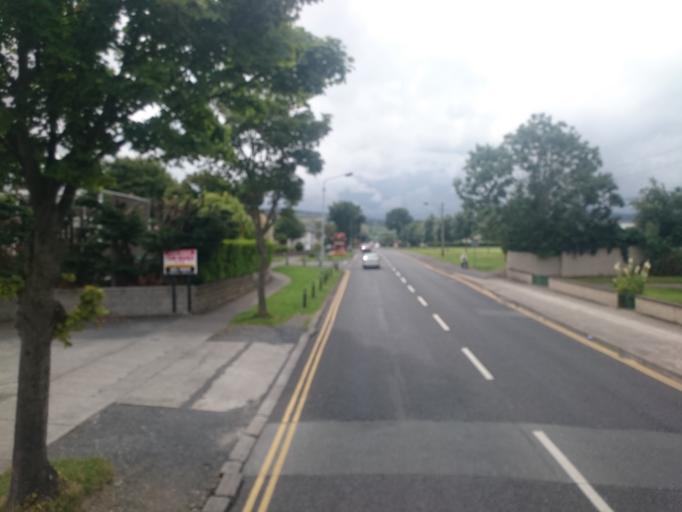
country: IE
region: Leinster
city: Oldbawn
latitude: 53.2824
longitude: -6.3593
